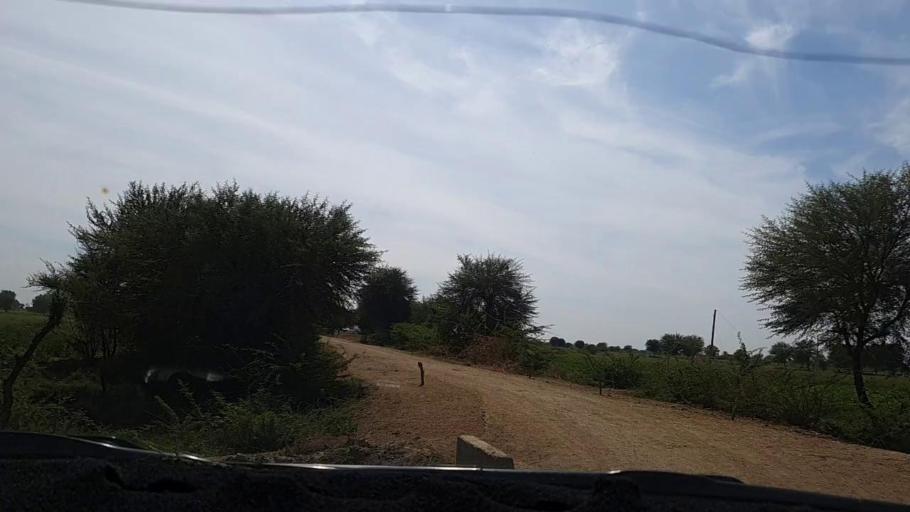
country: PK
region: Sindh
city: Pithoro
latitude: 25.5061
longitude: 69.4593
